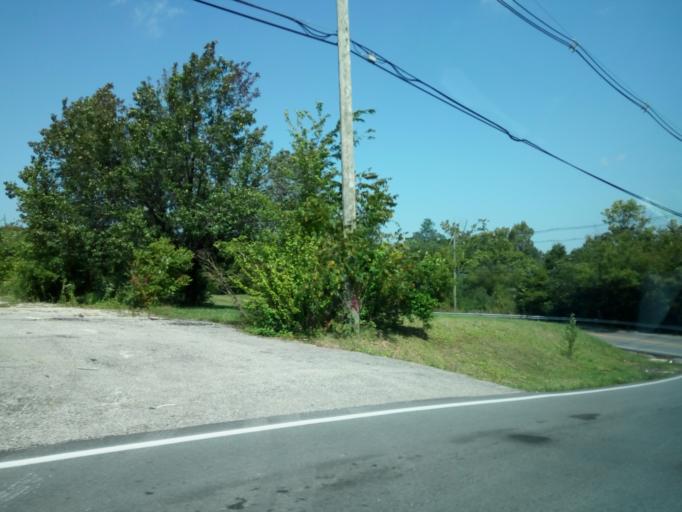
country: US
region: Kentucky
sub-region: Oldham County
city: Pewee Valley
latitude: 38.2825
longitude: -85.4853
